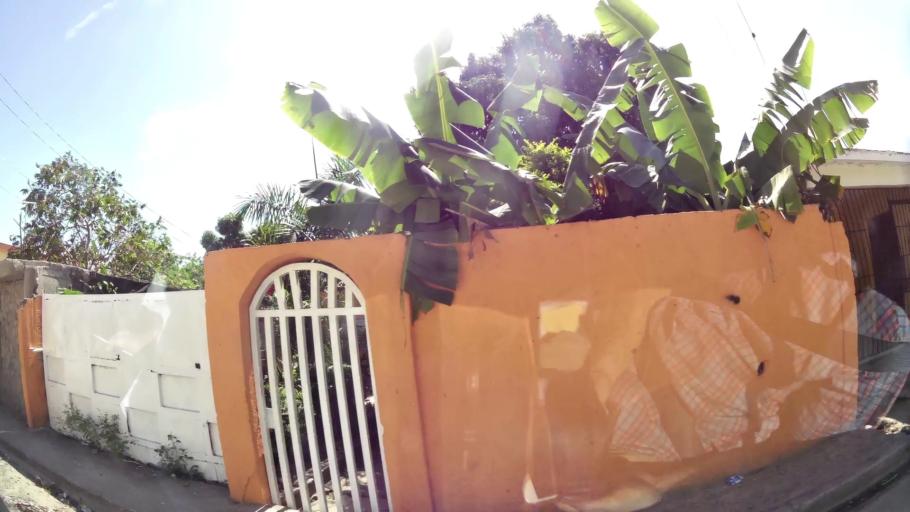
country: DO
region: San Cristobal
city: San Cristobal
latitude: 18.4228
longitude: -70.1034
